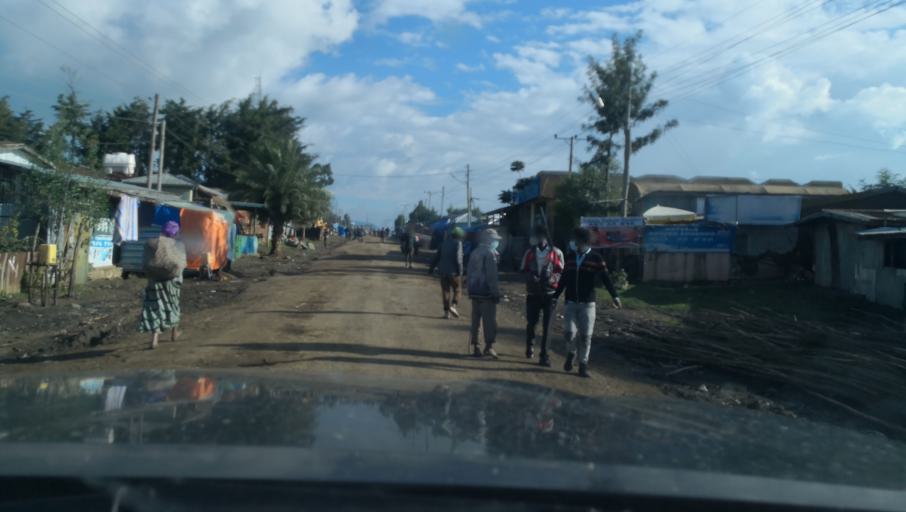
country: ET
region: Oromiya
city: Tulu Bolo
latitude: 8.4651
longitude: 38.2524
